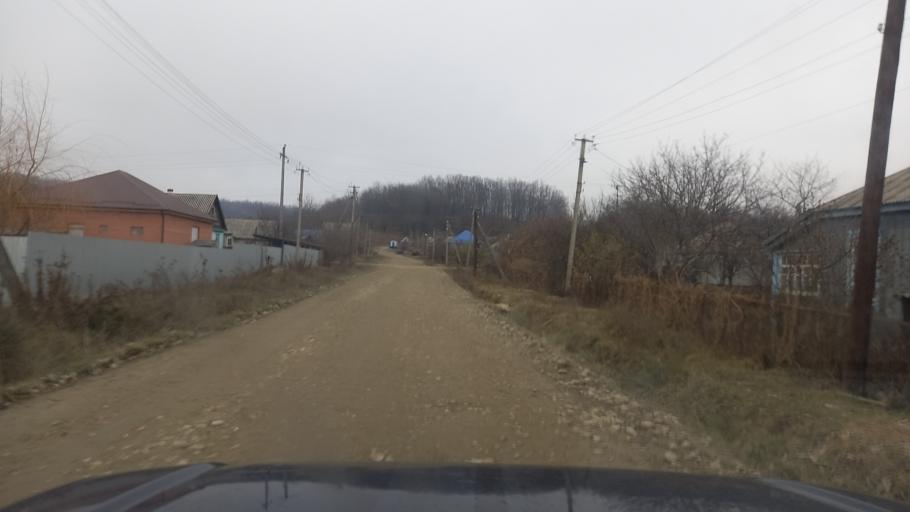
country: RU
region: Krasnodarskiy
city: Neftegorsk
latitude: 44.2492
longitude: 39.7589
